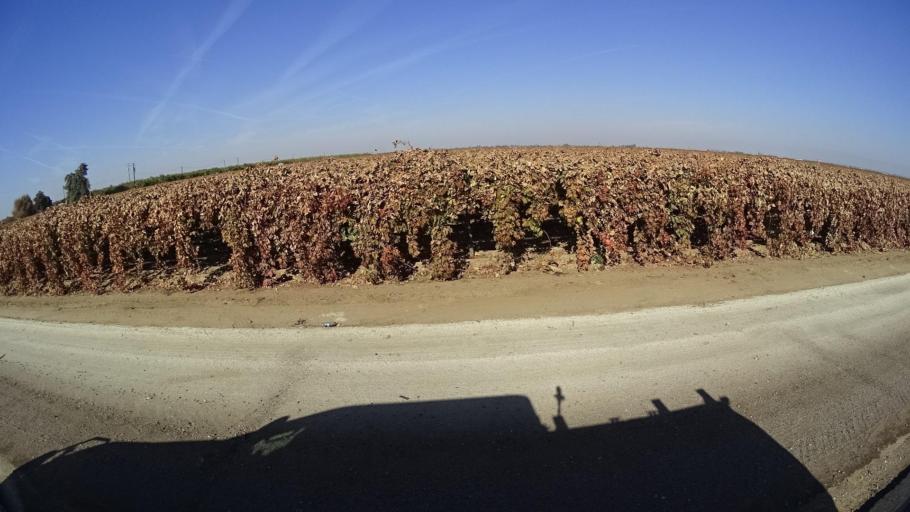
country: US
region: California
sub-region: Kern County
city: McFarland
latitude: 35.6454
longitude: -119.2304
